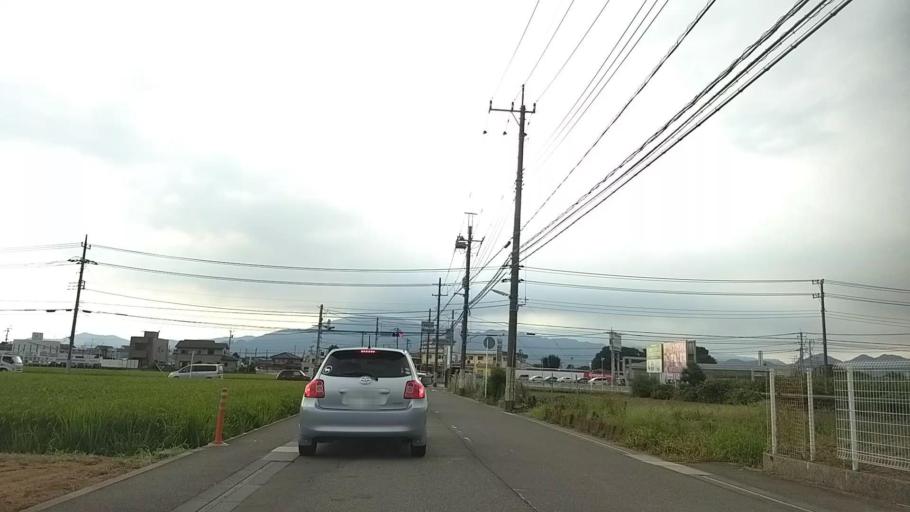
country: JP
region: Kanagawa
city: Atsugi
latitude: 35.4539
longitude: 139.3843
